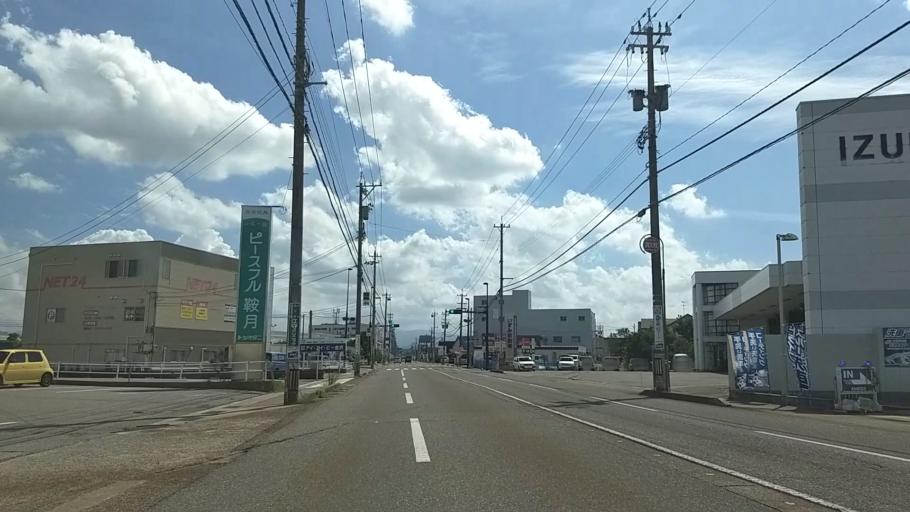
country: JP
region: Ishikawa
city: Kanazawa-shi
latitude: 36.6147
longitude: 136.6312
